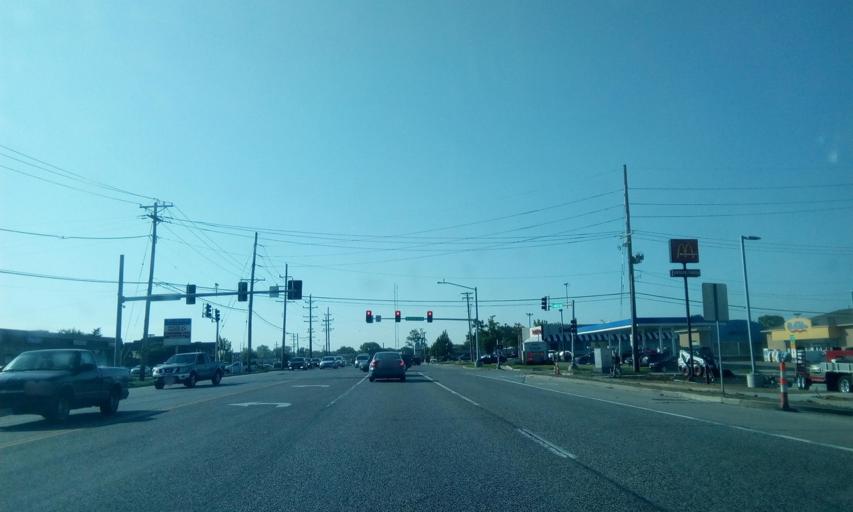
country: US
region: Missouri
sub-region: Saint Louis County
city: Green Park
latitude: 38.5215
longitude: -90.3464
